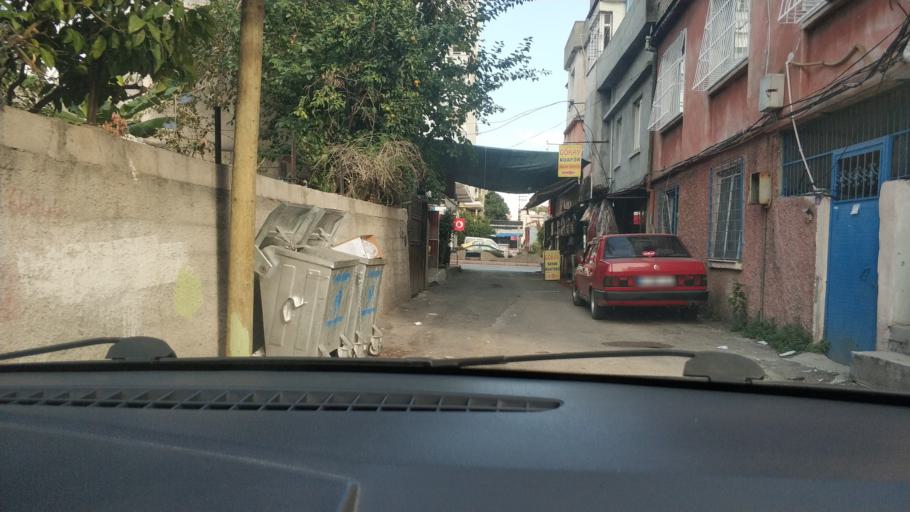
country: TR
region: Adana
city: Adana
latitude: 37.0080
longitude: 35.3231
